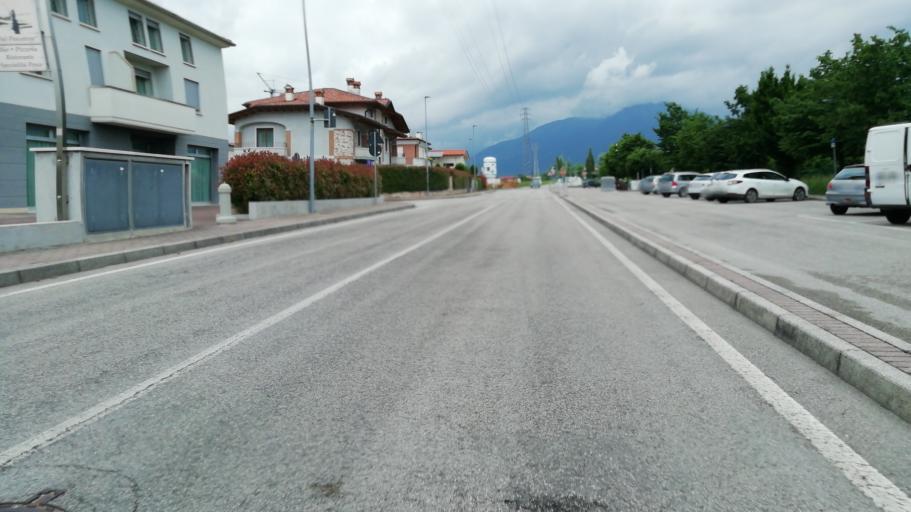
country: IT
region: Veneto
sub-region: Provincia di Vicenza
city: Centrale
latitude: 45.7253
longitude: 11.4799
